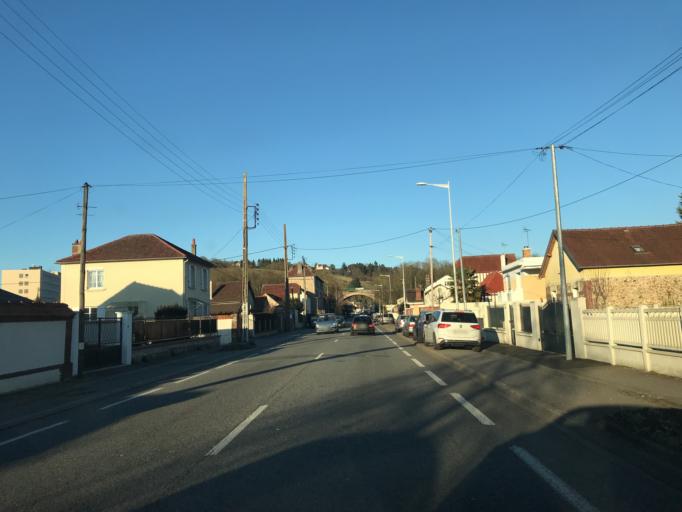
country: FR
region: Haute-Normandie
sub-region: Departement de l'Eure
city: Evreux
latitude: 49.0214
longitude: 1.1220
